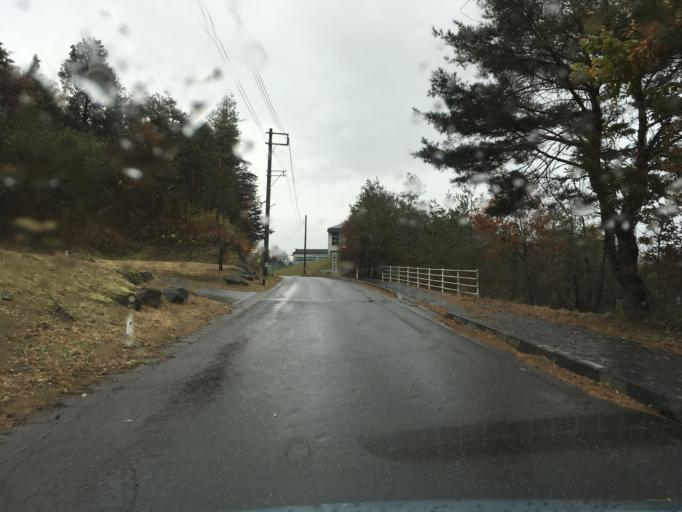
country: JP
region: Iwate
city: Ichinoseki
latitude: 38.7801
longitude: 141.2348
